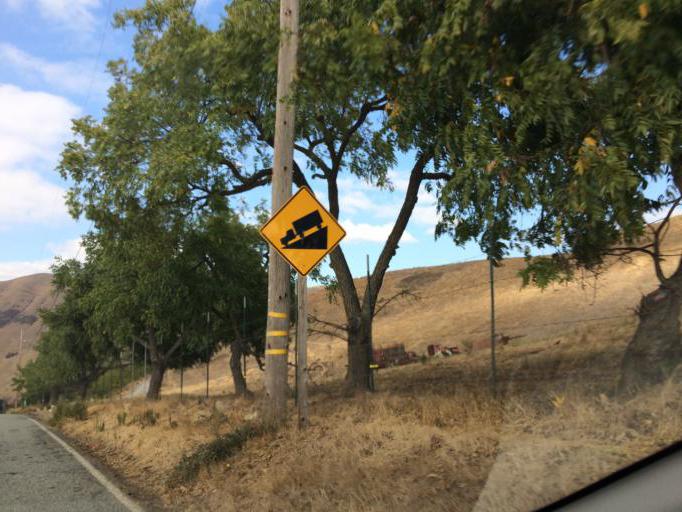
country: US
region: California
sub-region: Santa Clara County
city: East Foothills
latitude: 37.3871
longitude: -121.8020
